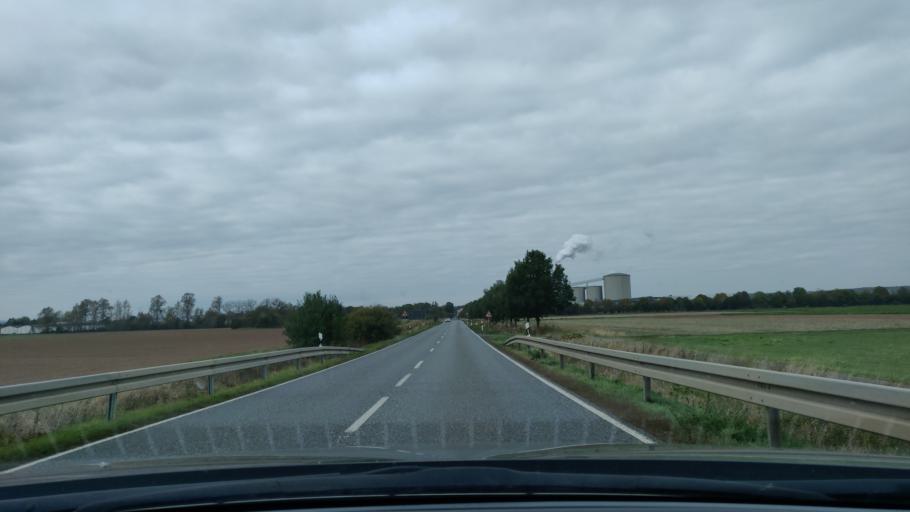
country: DE
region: Hesse
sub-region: Regierungsbezirk Kassel
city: Wabern
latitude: 51.0954
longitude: 9.3677
